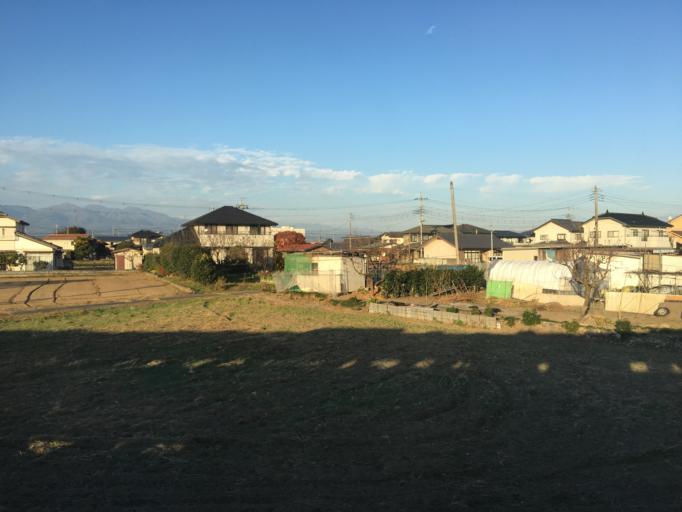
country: JP
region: Gunma
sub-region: Sawa-gun
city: Tamamura
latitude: 36.3522
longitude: 139.1445
